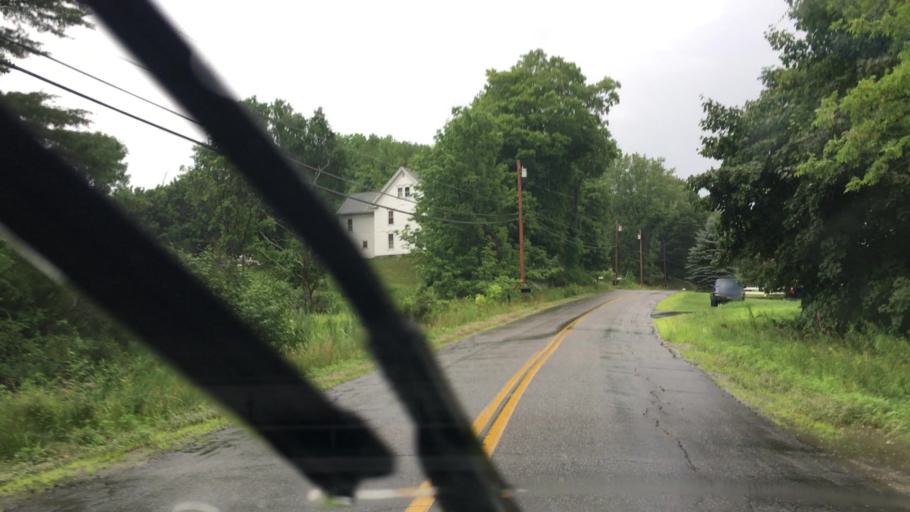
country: US
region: Maine
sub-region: Kennebec County
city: Gardiner
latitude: 44.2115
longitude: -69.8065
